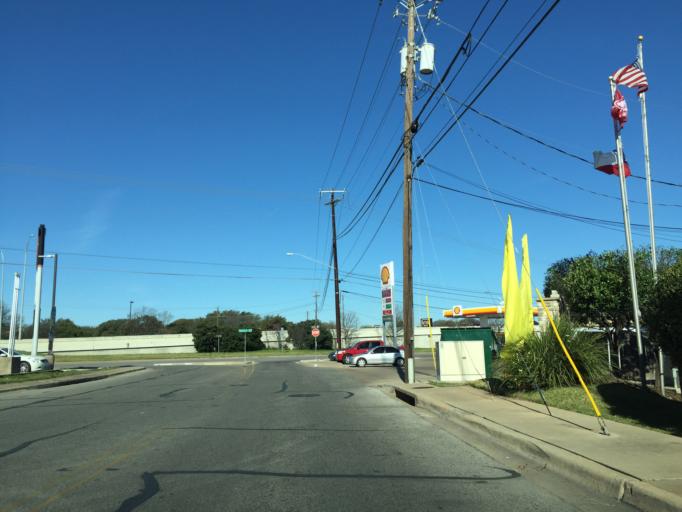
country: US
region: Texas
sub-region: Williamson County
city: Jollyville
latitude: 30.4166
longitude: -97.7453
